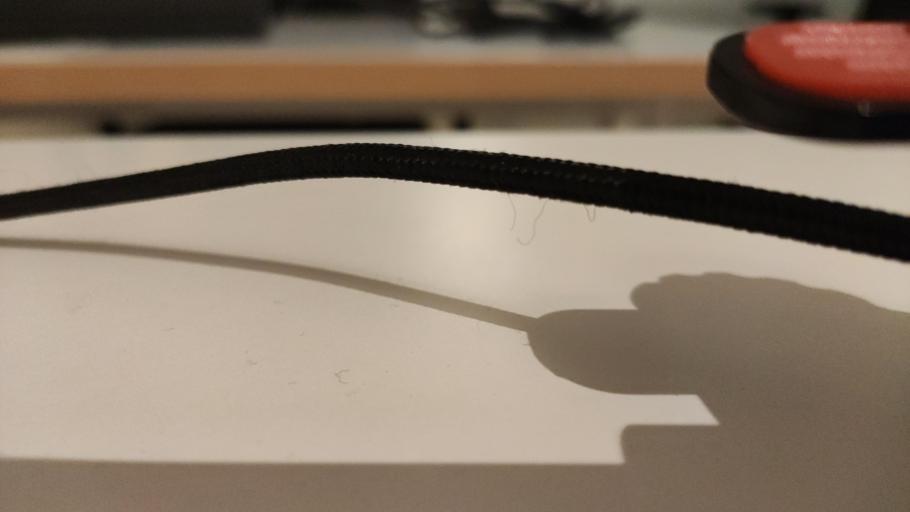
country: RU
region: Moskovskaya
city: Kurovskoye
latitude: 55.5918
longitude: 38.9227
